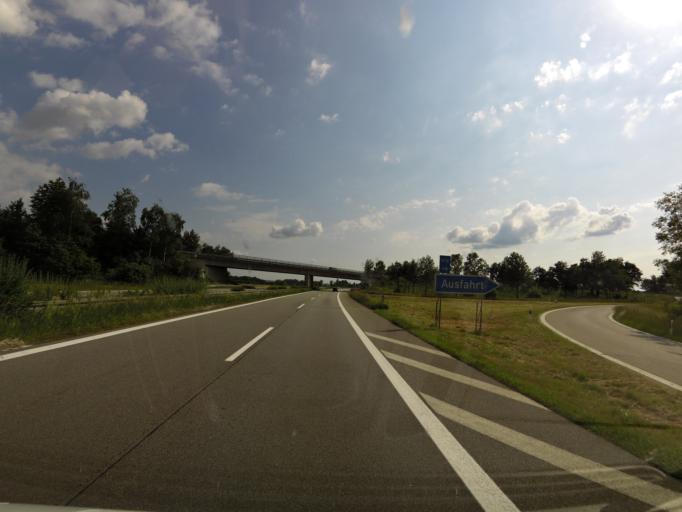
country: DE
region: Bavaria
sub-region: Lower Bavaria
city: Wallersdorf
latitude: 48.7279
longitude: 12.7286
